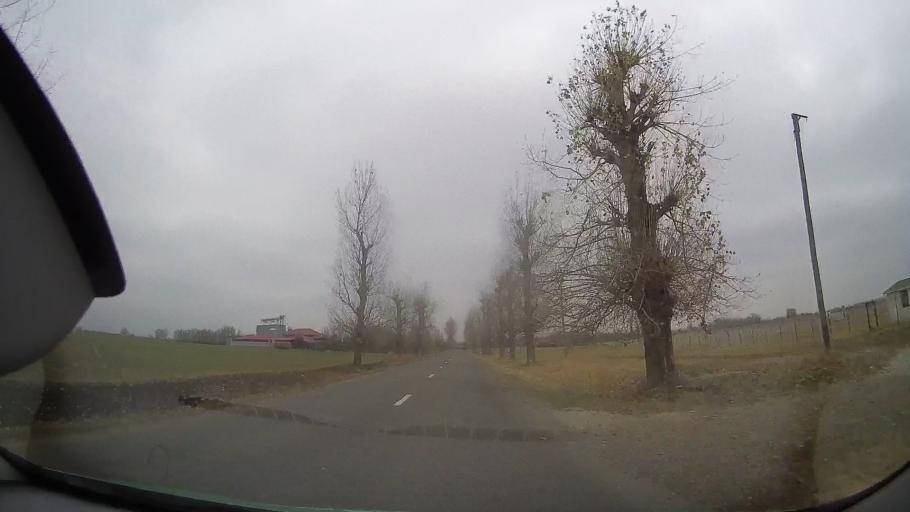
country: RO
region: Ialomita
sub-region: Comuna Grindu
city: Grindu
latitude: 44.7837
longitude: 26.9044
